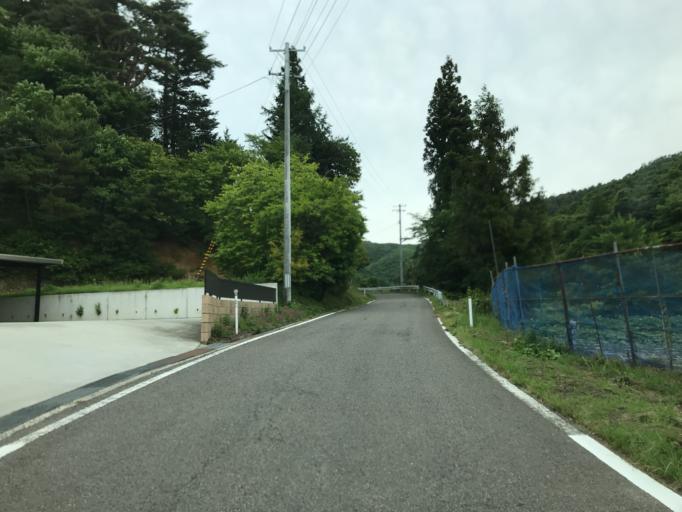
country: JP
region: Fukushima
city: Funehikimachi-funehiki
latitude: 37.4206
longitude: 140.7110
